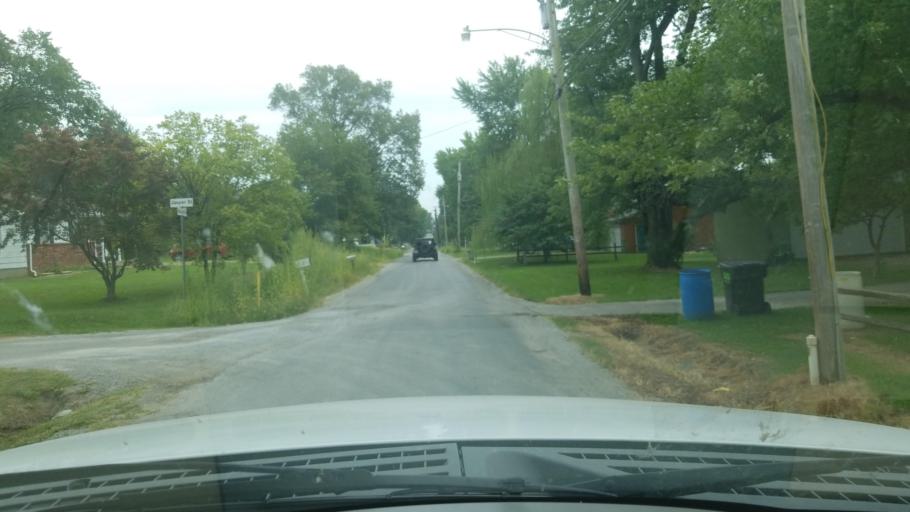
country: US
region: Illinois
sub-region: Saline County
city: Eldorado
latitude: 37.8213
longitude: -88.4477
